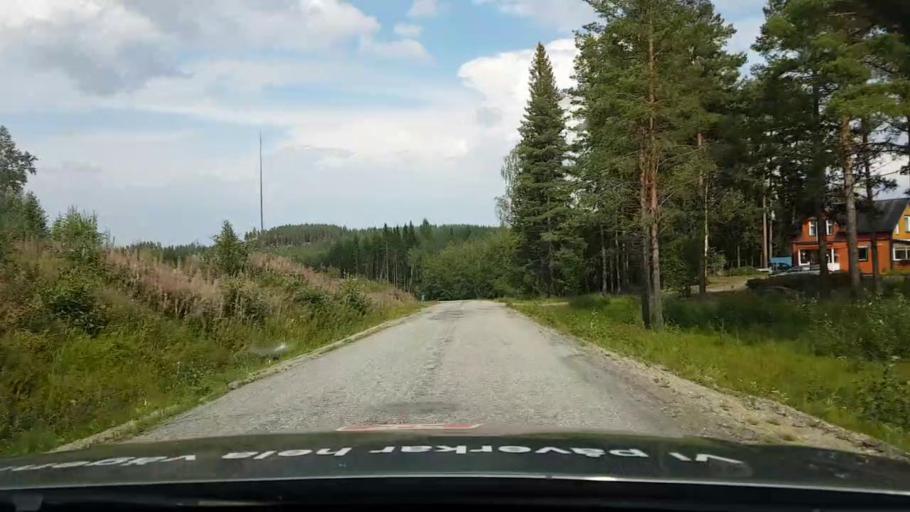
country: SE
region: Vaesternorrland
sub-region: Ange Kommun
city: Fransta
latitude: 62.7795
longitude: 15.9918
